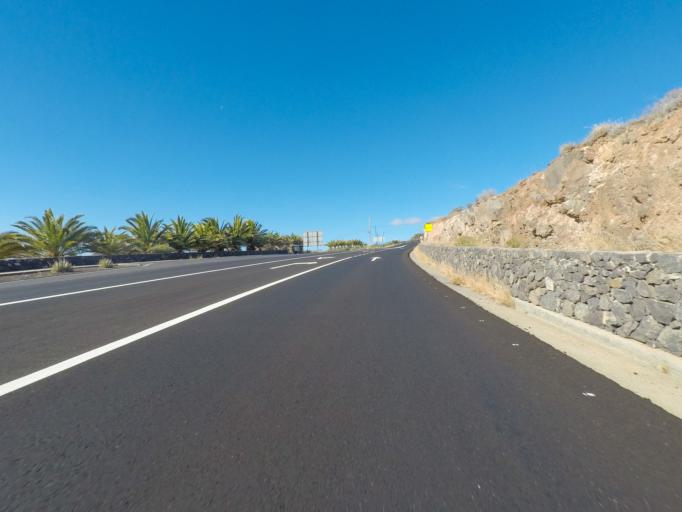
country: ES
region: Canary Islands
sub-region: Provincia de Santa Cruz de Tenerife
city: Alajero
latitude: 28.0449
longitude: -17.1958
